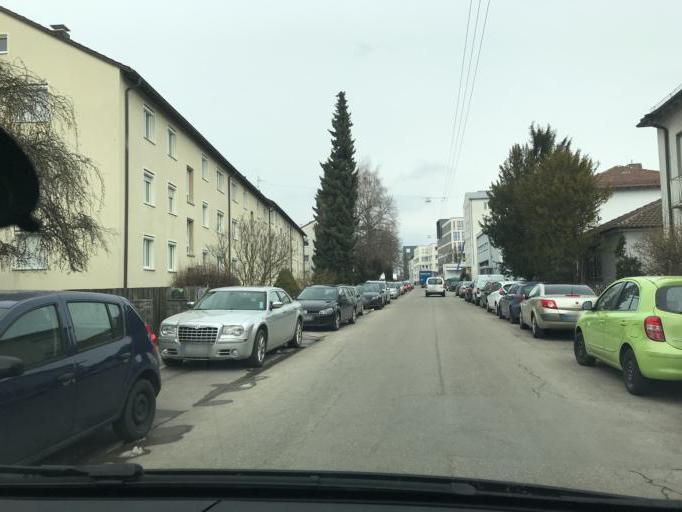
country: DE
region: Baden-Wuerttemberg
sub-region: Regierungsbezirk Stuttgart
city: Steinenbronn
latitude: 48.7234
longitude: 9.1160
